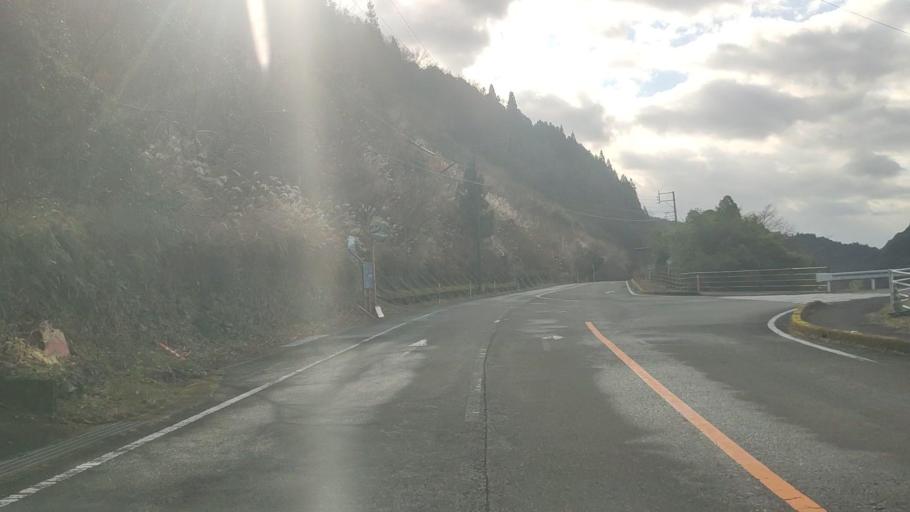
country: JP
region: Kumamoto
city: Hitoyoshi
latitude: 32.3125
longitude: 130.8477
